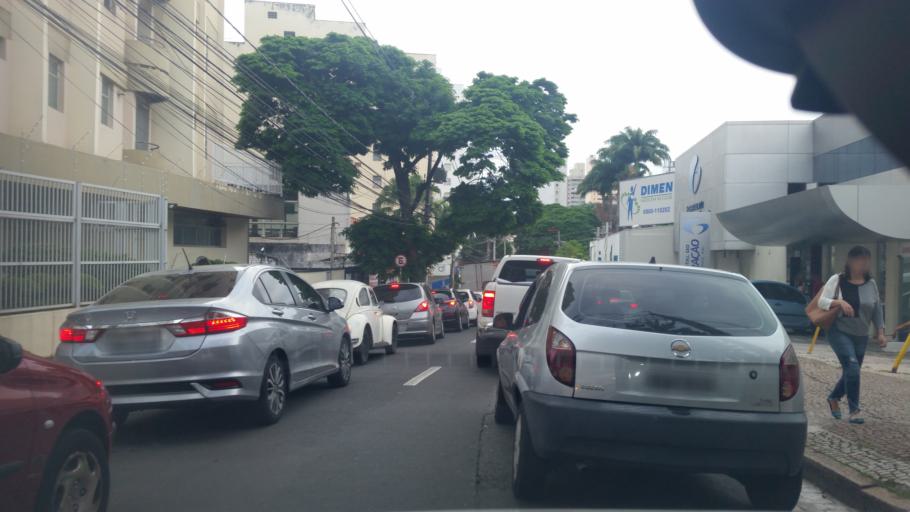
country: BR
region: Sao Paulo
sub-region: Campinas
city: Campinas
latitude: -22.9012
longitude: -47.0552
